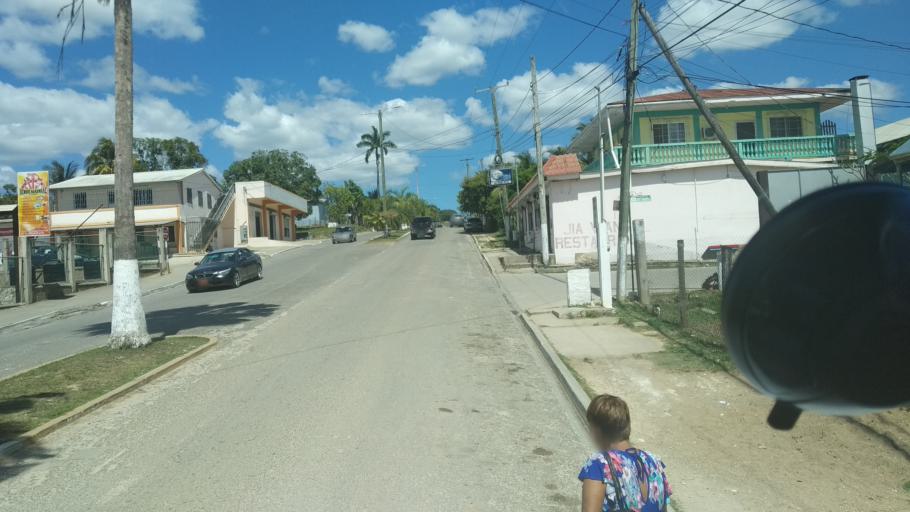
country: BZ
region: Cayo
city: Benque Viejo del Carmen
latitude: 17.0731
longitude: -89.1366
